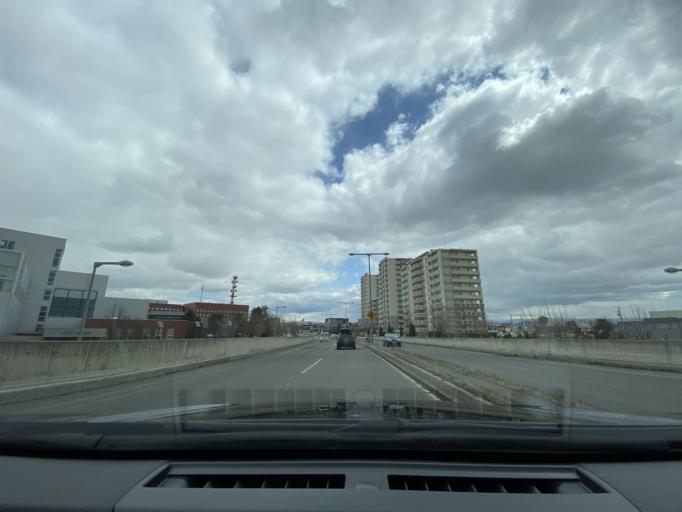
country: JP
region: Hokkaido
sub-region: Asahikawa-shi
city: Asahikawa
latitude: 43.7556
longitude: 142.3702
